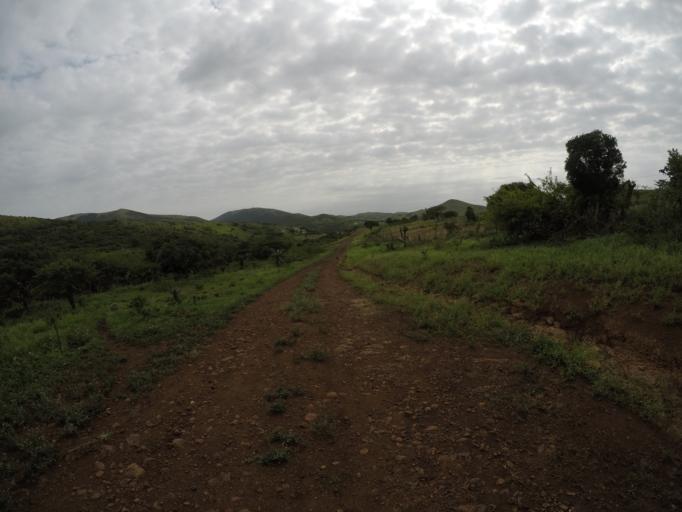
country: ZA
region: KwaZulu-Natal
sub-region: uThungulu District Municipality
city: Empangeni
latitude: -28.6286
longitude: 31.9071
